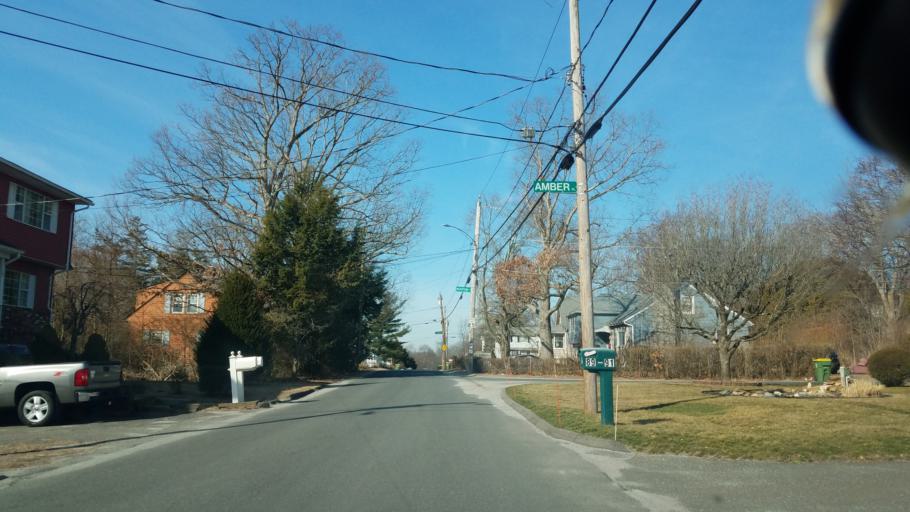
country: US
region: Connecticut
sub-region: New Haven County
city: Wolcott
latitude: 41.5545
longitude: -72.9876
